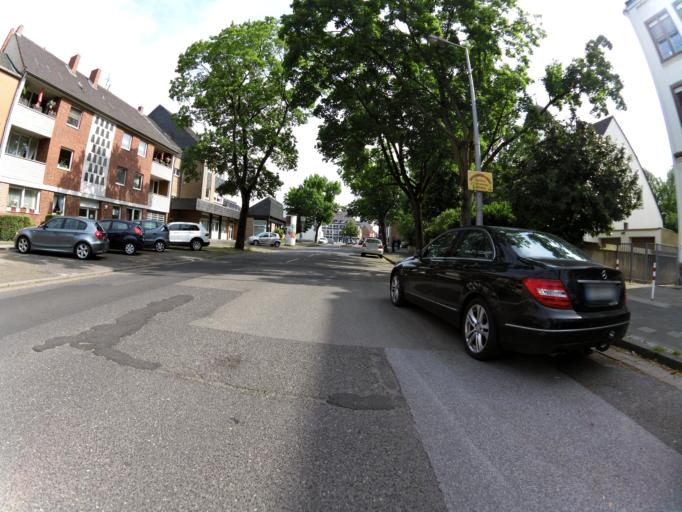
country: DE
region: North Rhine-Westphalia
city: Julich
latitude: 50.9250
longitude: 6.3565
